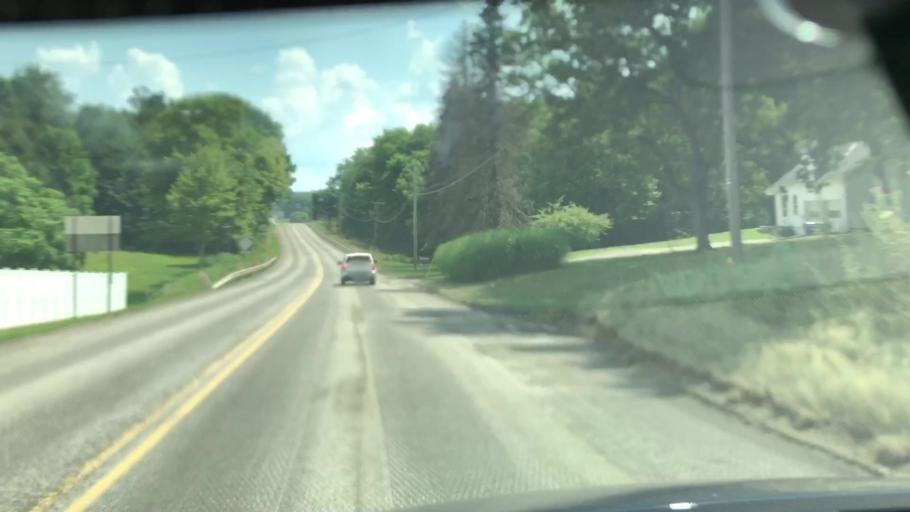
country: US
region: Pennsylvania
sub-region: Butler County
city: Saxonburg
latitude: 40.7970
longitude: -79.8199
